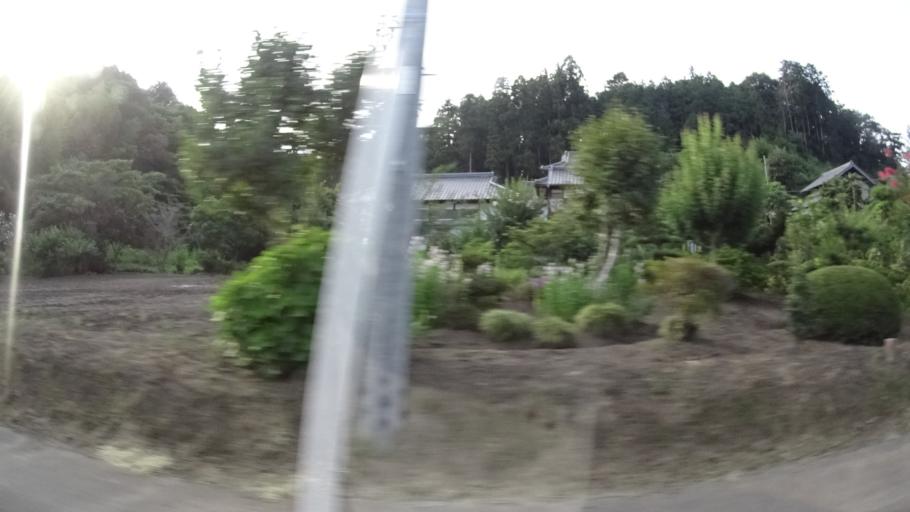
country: JP
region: Tochigi
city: Karasuyama
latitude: 36.5842
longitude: 140.1116
